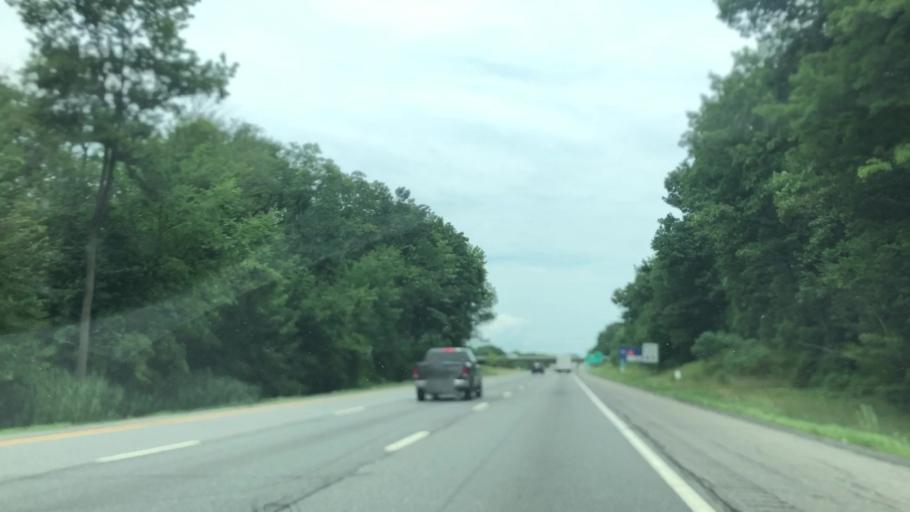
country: US
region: New York
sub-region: Saratoga County
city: Country Knolls
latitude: 42.8495
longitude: -73.7727
